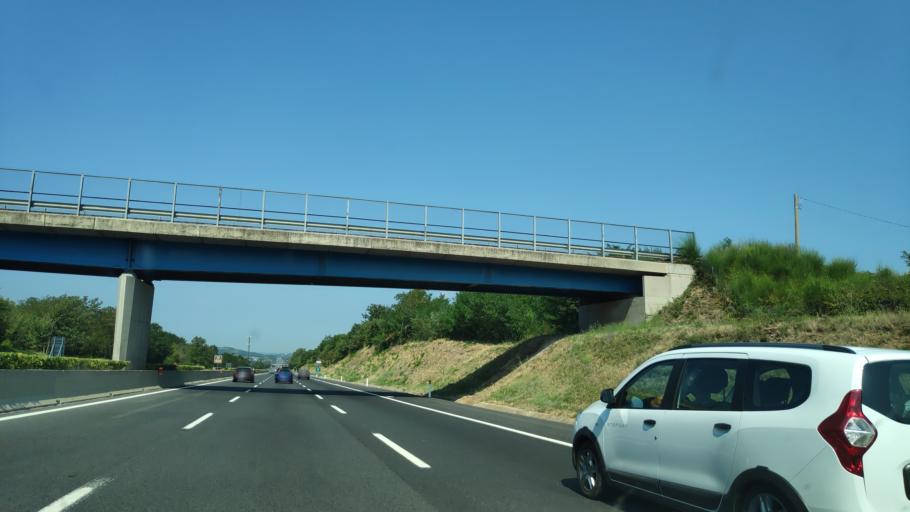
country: IT
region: Campania
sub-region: Provincia di Caserta
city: San Pietro Infine
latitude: 41.4140
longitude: 13.9463
